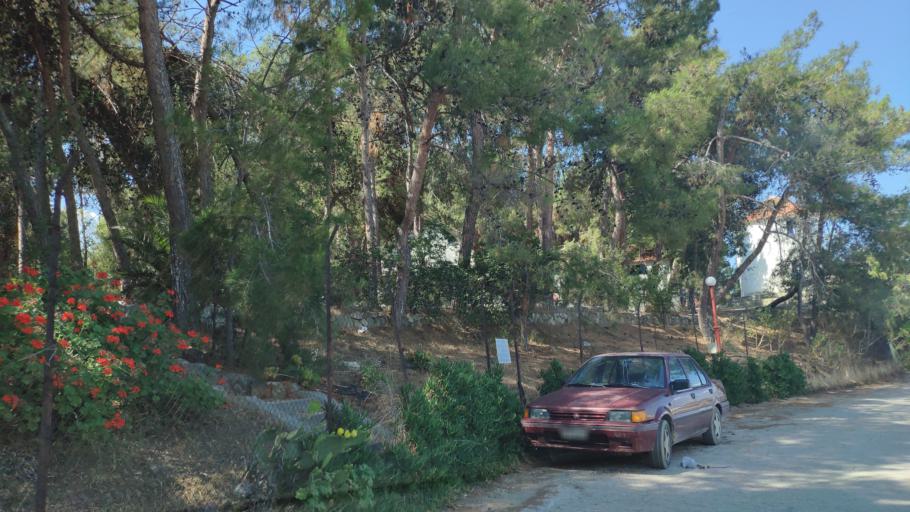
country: GR
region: Central Greece
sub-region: Nomos Evvoias
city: Eretria
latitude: 38.3856
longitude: 23.8007
